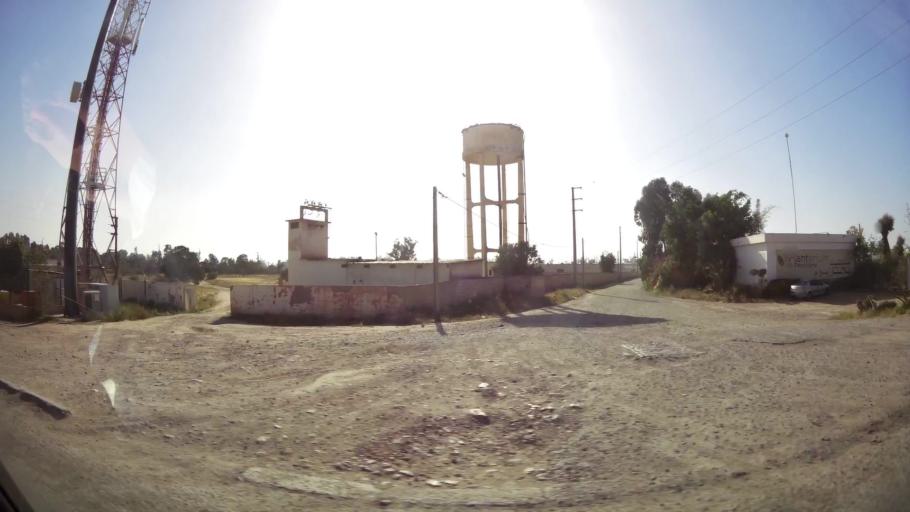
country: MA
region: Souss-Massa-Draa
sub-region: Inezgane-Ait Mellou
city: Inezgane
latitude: 30.3609
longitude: -9.5060
